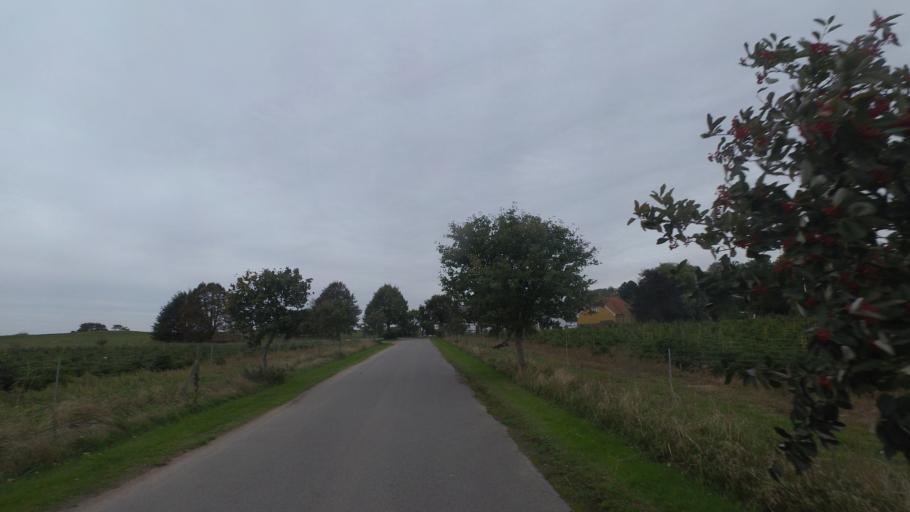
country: DK
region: Capital Region
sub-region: Bornholm Kommune
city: Akirkeby
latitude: 55.0020
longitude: 14.9999
